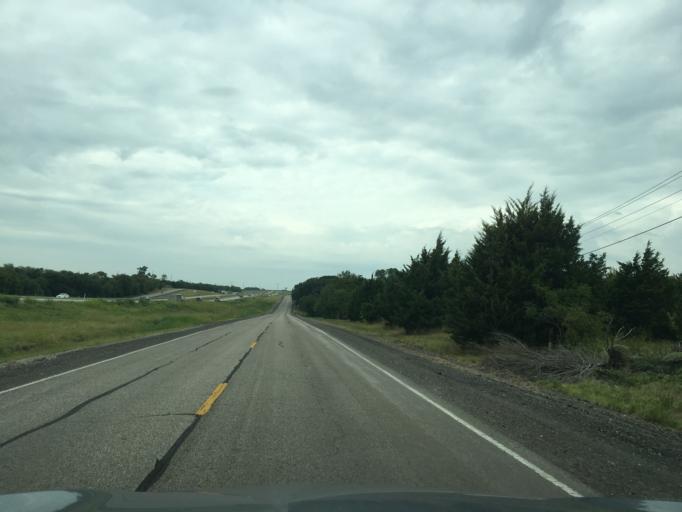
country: US
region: Texas
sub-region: Grayson County
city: Van Alstyne
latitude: 33.3960
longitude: -96.5809
